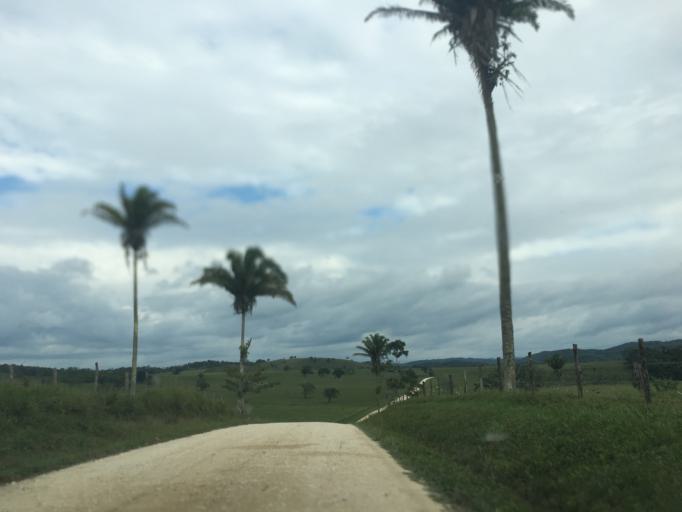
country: BZ
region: Cayo
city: Benque Viejo del Carmen
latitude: 17.1121
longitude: -89.1236
